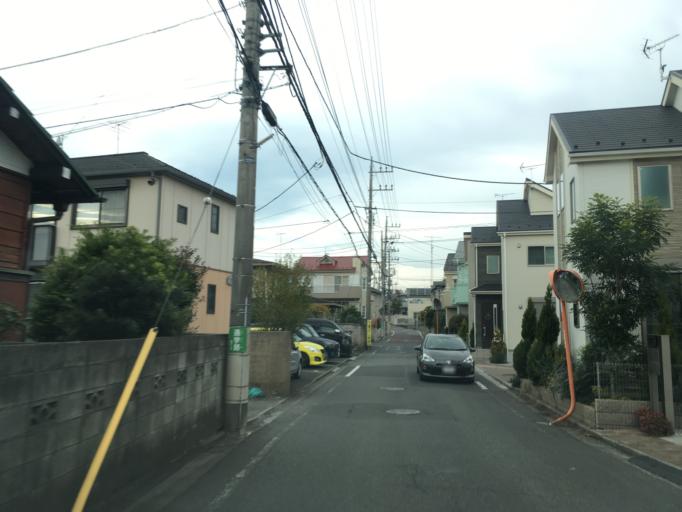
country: JP
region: Tokyo
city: Higashimurayama-shi
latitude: 35.7584
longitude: 139.4559
